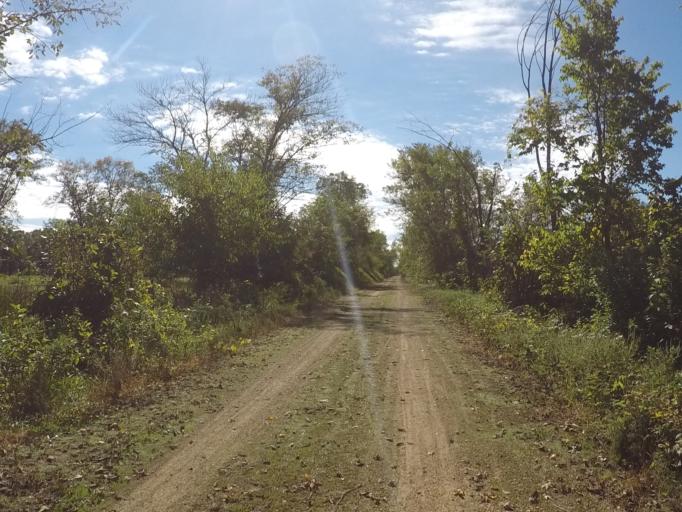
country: US
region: Wisconsin
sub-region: Richland County
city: Richland Center
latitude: 43.2791
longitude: -90.3157
